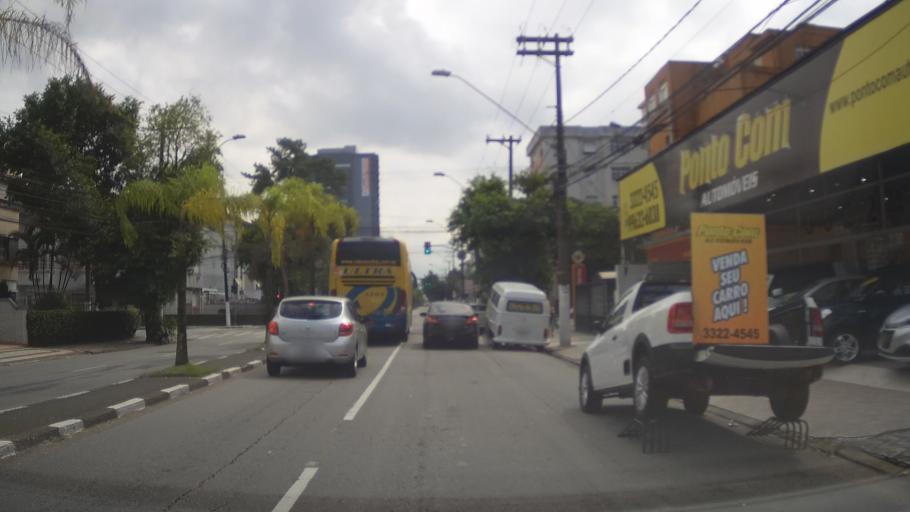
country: BR
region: Sao Paulo
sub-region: Santos
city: Santos
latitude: -23.9571
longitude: -46.3243
